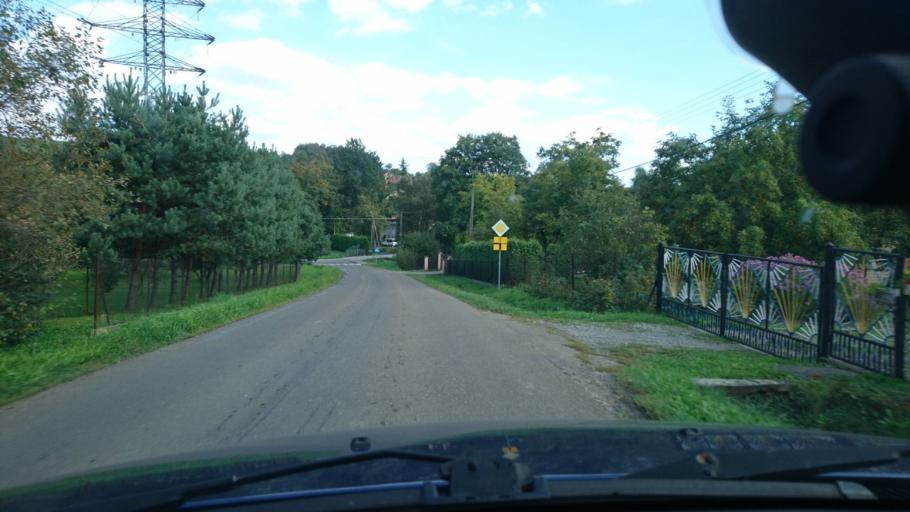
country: PL
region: Silesian Voivodeship
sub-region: Powiat bielski
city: Jasienica
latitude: 49.8301
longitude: 18.9403
